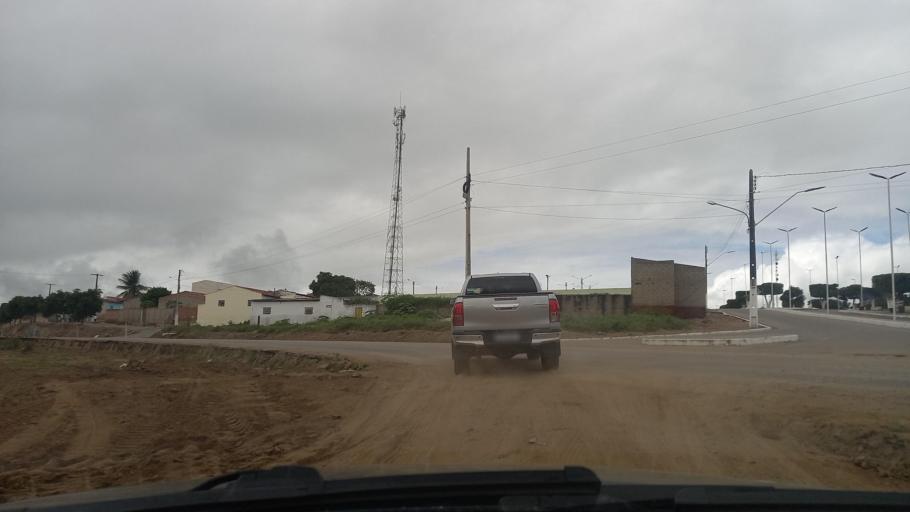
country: BR
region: Alagoas
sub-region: Batalha
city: Batalha
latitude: -9.6309
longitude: -37.2073
